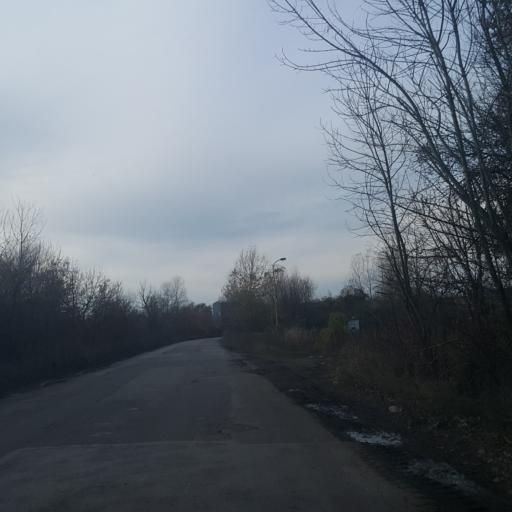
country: RS
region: Central Serbia
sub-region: Belgrade
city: Lazarevac
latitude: 44.4234
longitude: 20.2900
